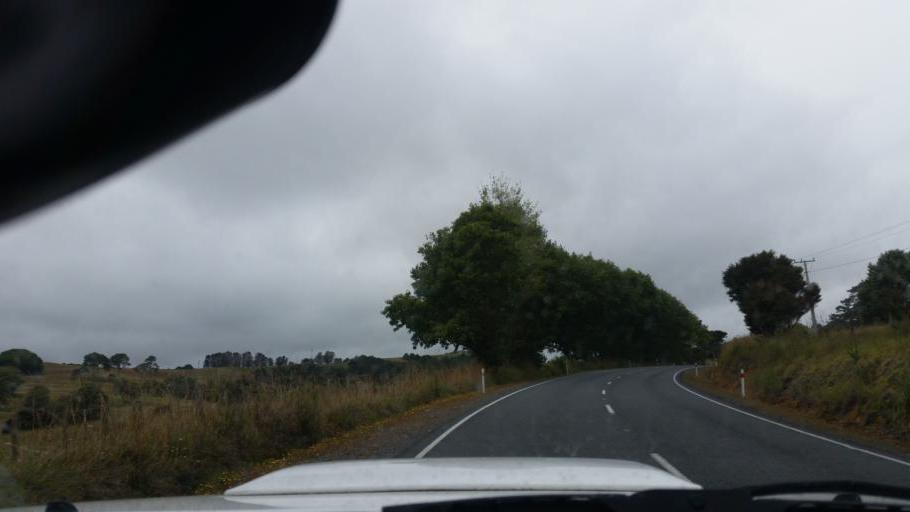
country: NZ
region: Auckland
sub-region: Auckland
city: Wellsford
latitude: -36.1362
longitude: 174.5186
